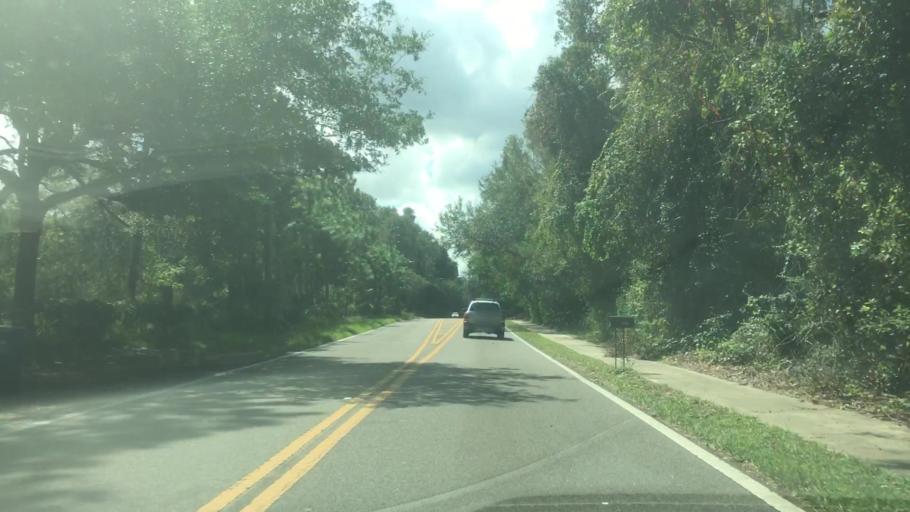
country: US
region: Florida
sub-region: Duval County
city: Jacksonville
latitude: 30.4470
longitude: -81.5792
